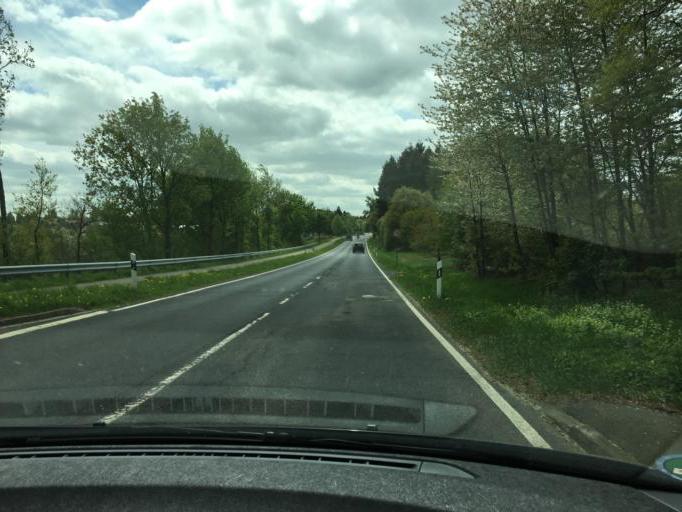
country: DE
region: Rheinland-Pfalz
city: Kirchsahr
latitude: 50.5224
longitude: 6.8603
